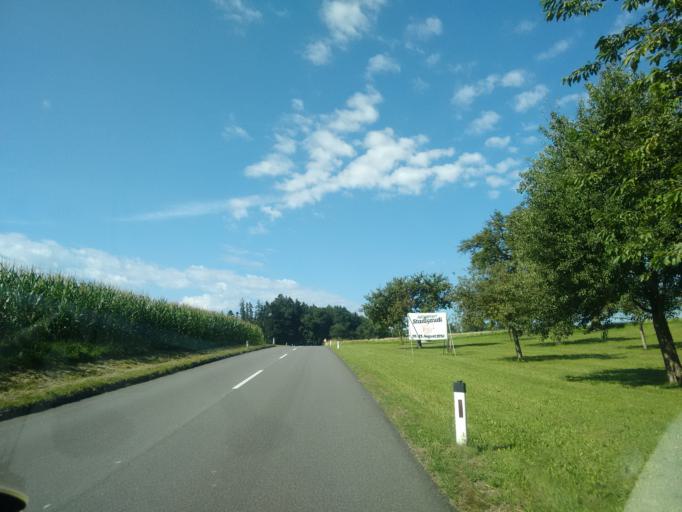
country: AT
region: Upper Austria
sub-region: Politischer Bezirk Steyr-Land
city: Pfarrkirchen bei Bad Hall
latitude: 48.0055
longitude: 14.1746
